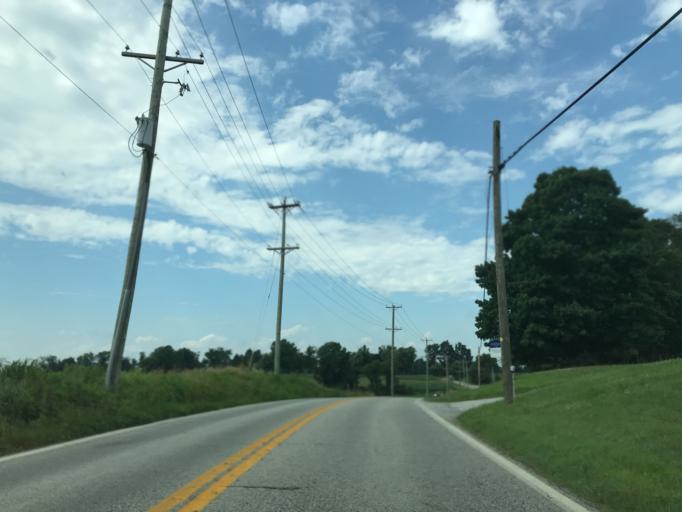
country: US
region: Maryland
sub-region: Harford County
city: Jarrettsville
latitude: 39.6647
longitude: -76.4079
